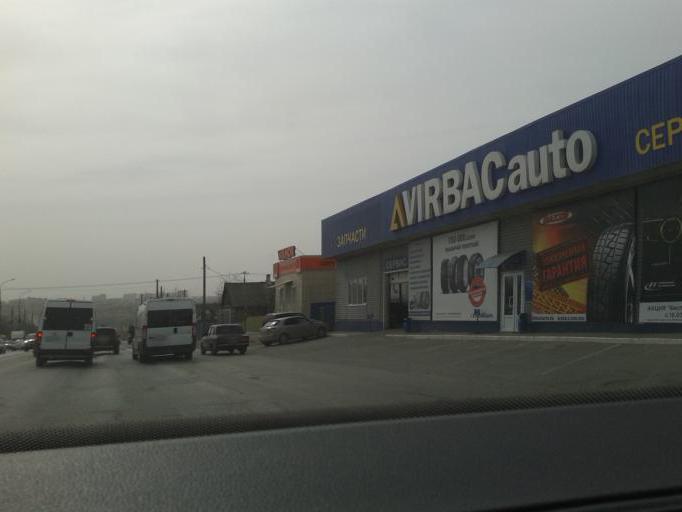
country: RU
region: Volgograd
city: Volgograd
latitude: 48.6917
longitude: 44.4612
